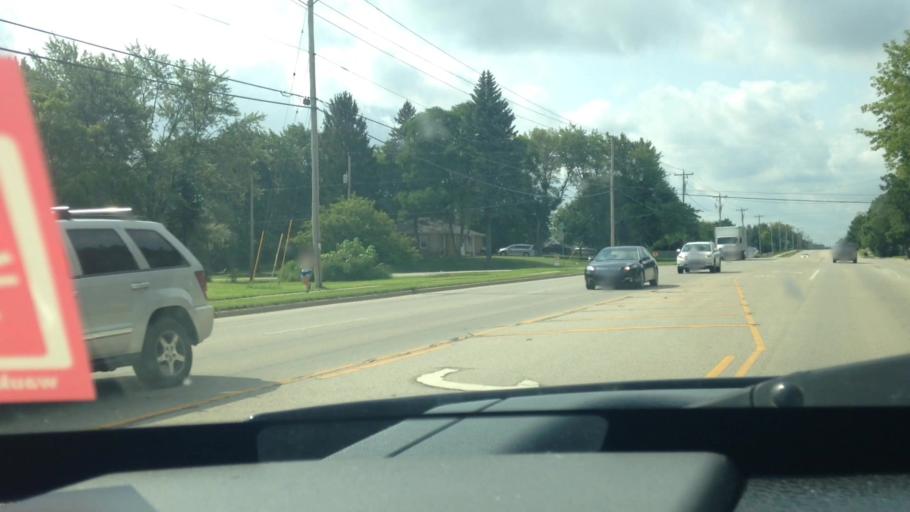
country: US
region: Wisconsin
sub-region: Waukesha County
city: Menomonee Falls
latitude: 43.1554
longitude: -88.1043
